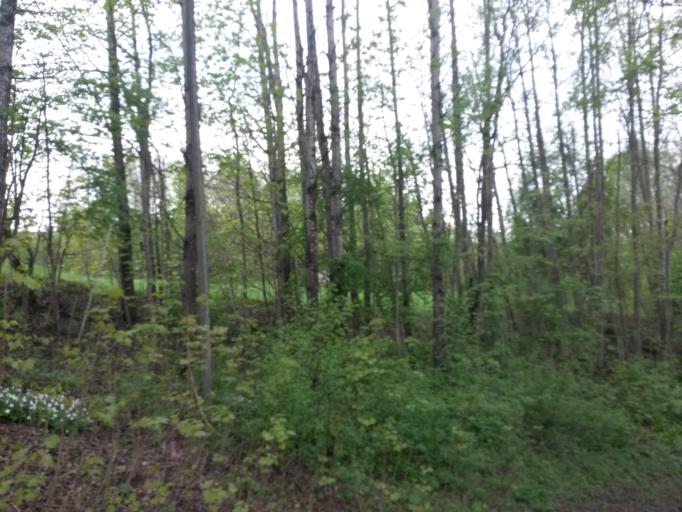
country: NO
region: Akershus
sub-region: Asker
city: Asker
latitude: 59.8352
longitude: 10.4058
